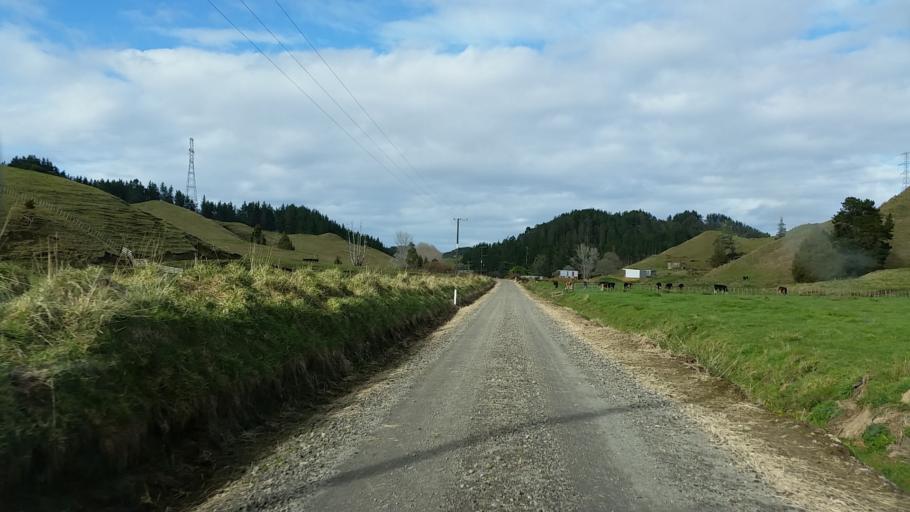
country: NZ
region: Taranaki
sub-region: South Taranaki District
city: Eltham
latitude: -39.2275
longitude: 174.5642
